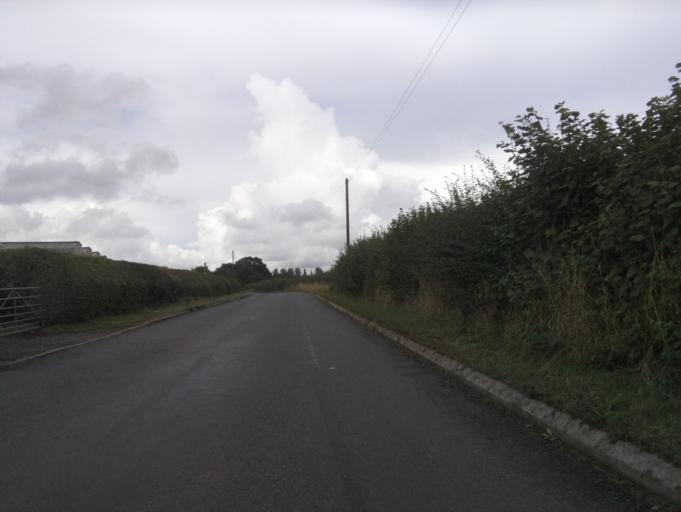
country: GB
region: England
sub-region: Worcestershire
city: Kidderminster
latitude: 52.3450
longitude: -2.1948
